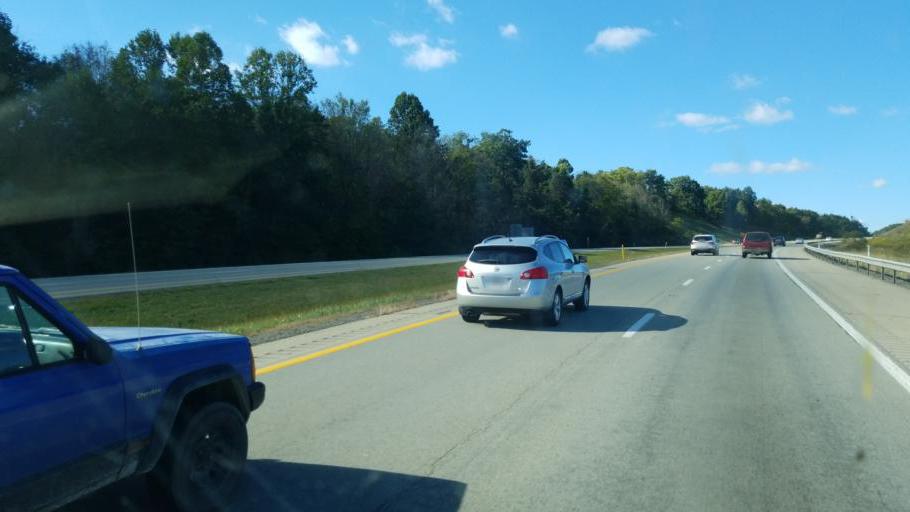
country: US
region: Pennsylvania
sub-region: Greene County
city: Morrisville
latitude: 39.8320
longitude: -80.1109
